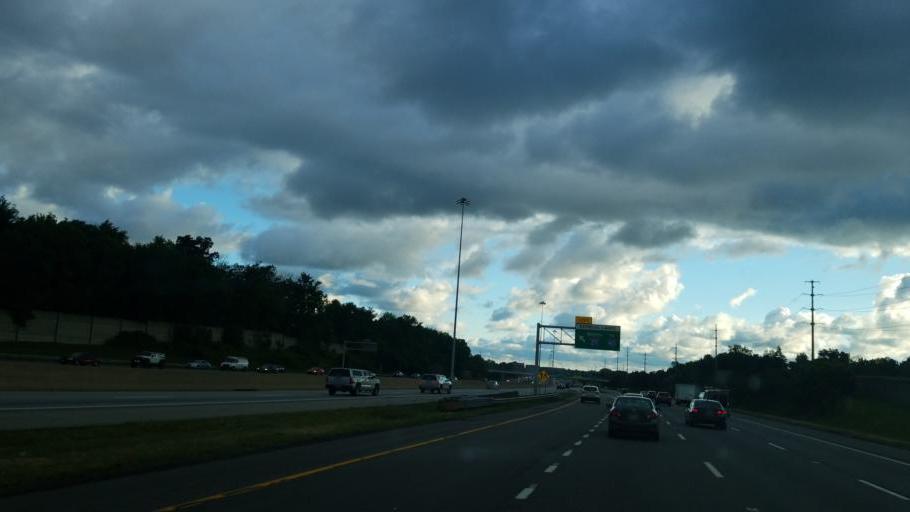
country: US
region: Ohio
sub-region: Cuyahoga County
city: Pepper Pike
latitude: 41.4802
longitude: -81.4869
